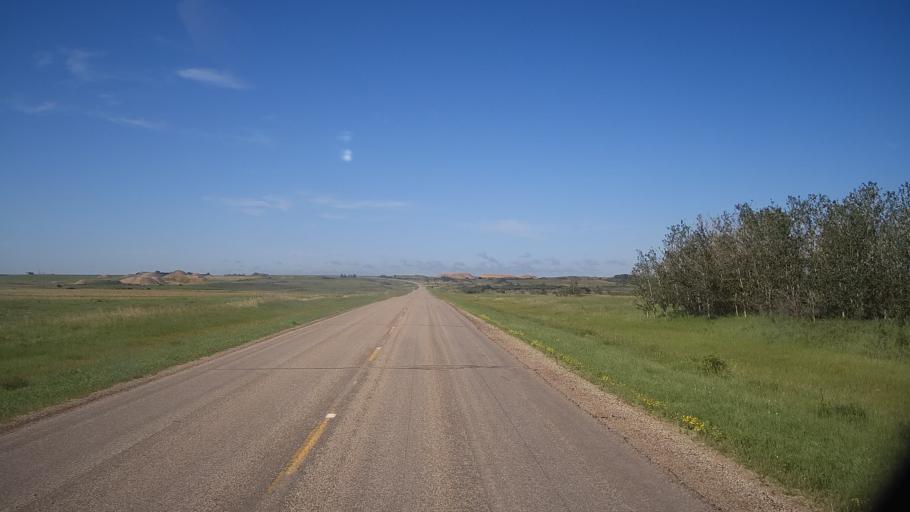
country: CA
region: Saskatchewan
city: Watrous
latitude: 51.7160
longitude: -105.3655
